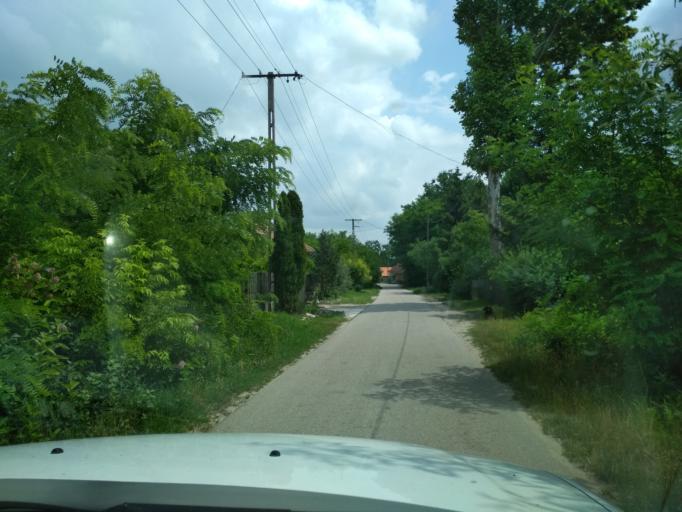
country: HU
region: Pest
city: Tapioszentmarton
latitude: 47.3700
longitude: 19.7612
